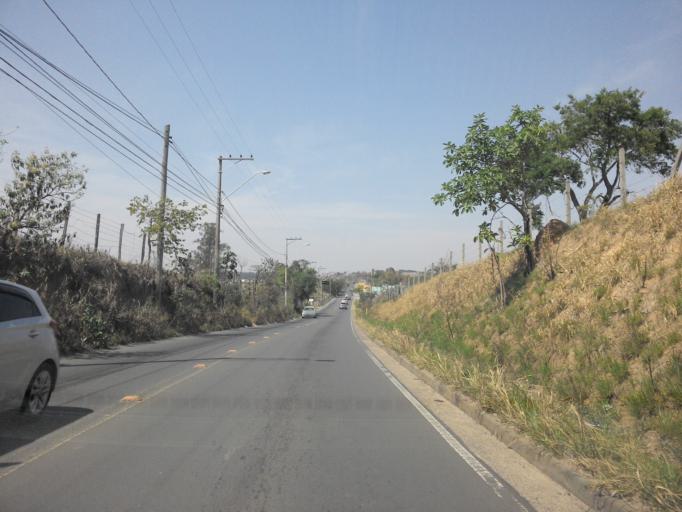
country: BR
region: Sao Paulo
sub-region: Hortolandia
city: Hortolandia
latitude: -22.9183
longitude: -47.1924
